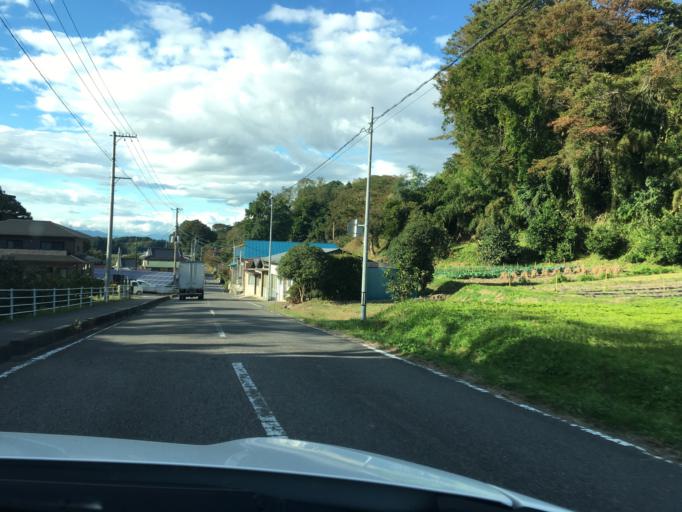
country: JP
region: Fukushima
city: Sukagawa
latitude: 37.2387
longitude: 140.4498
